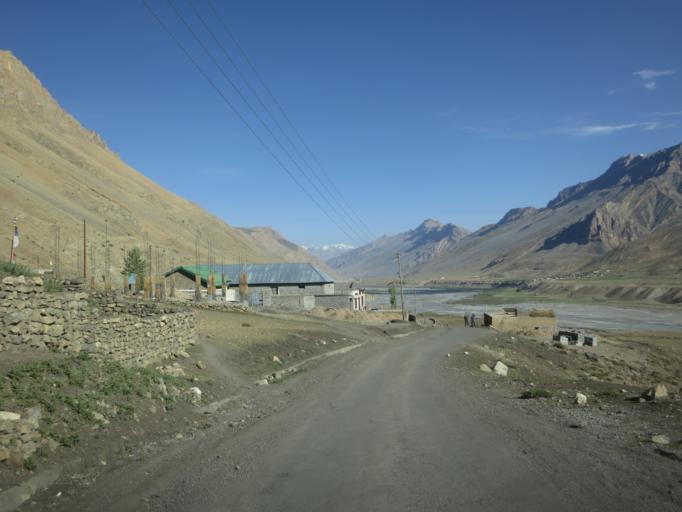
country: IN
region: Himachal Pradesh
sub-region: Shimla
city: Sarahan
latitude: 32.2899
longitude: 78.0129
